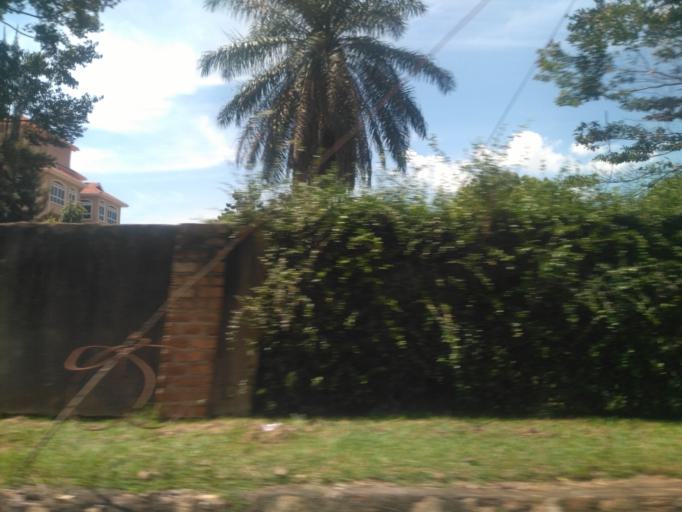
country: UG
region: Central Region
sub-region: Wakiso District
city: Entebbe
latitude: 0.0482
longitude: 32.4654
